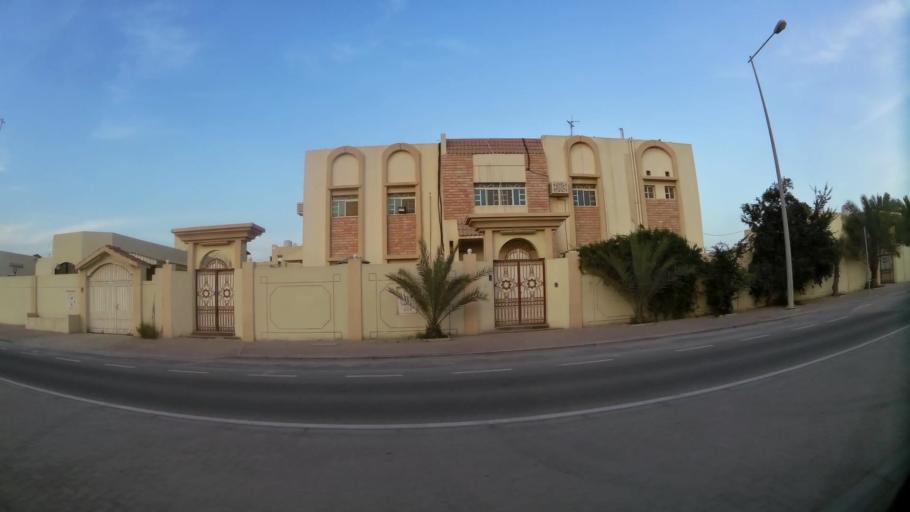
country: QA
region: Al Wakrah
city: Al Wakrah
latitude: 25.1875
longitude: 51.6074
